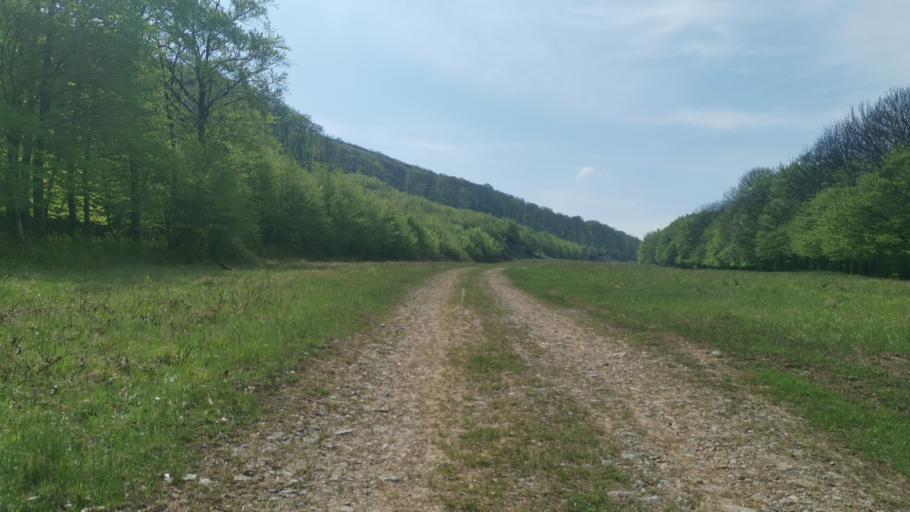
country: SK
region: Trnavsky
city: Smolenice
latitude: 48.5321
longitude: 17.4200
